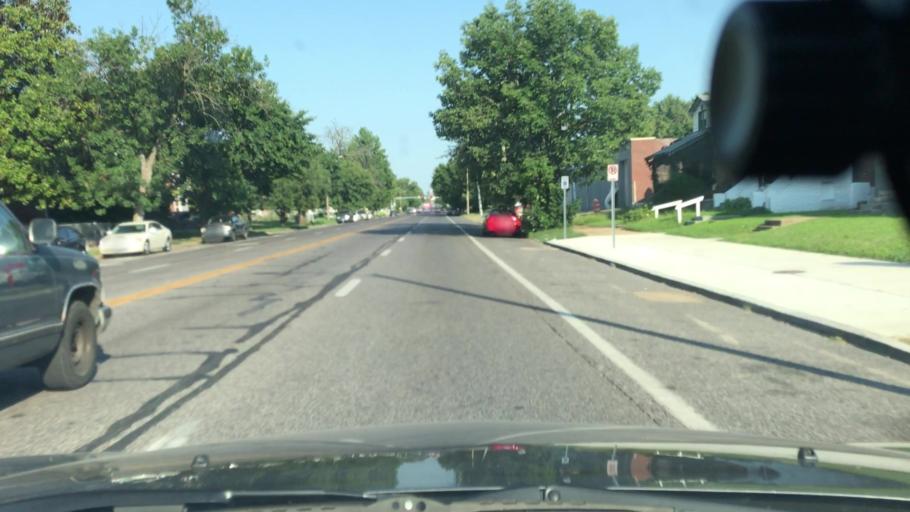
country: US
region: Missouri
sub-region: City of Saint Louis
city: St. Louis
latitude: 38.6502
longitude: -90.2371
